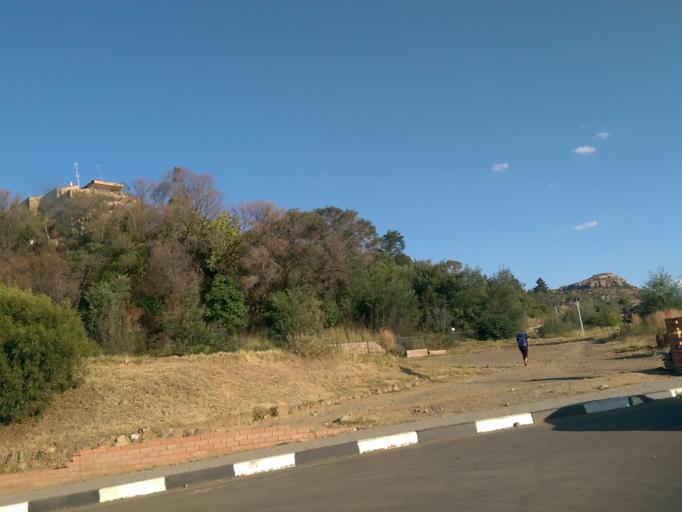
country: LS
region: Maseru
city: Maseru
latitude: -29.3177
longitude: 27.4866
